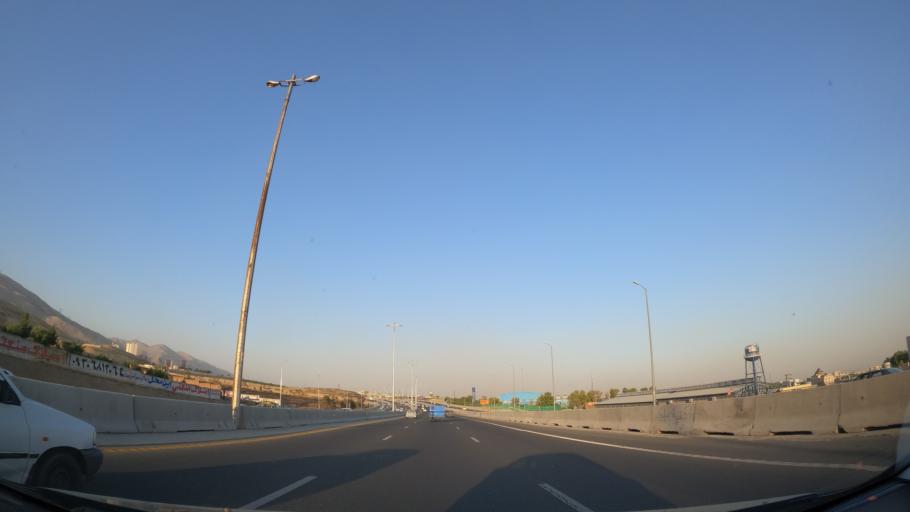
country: IR
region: Tehran
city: Shahr-e Qods
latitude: 35.7421
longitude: 51.1136
